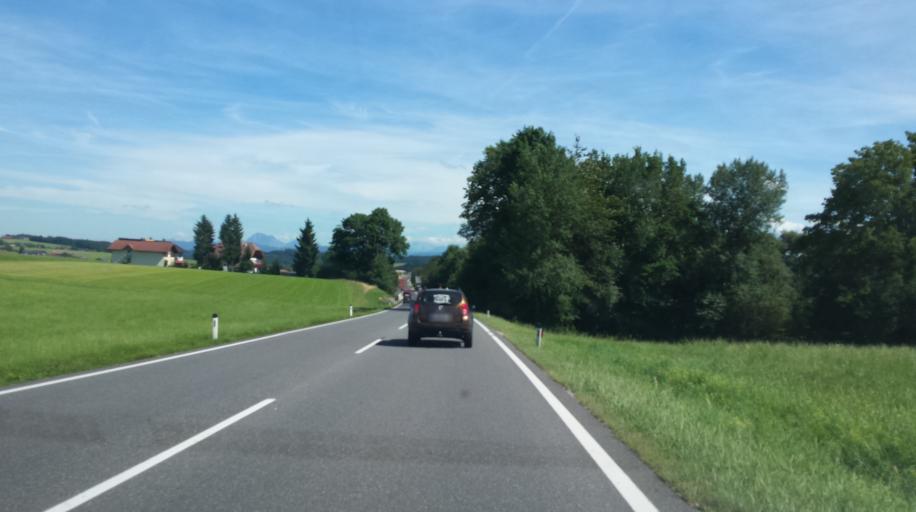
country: AT
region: Upper Austria
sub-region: Politischer Bezirk Vocklabruck
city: Oberhofen am Irrsee
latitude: 47.9964
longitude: 13.3451
